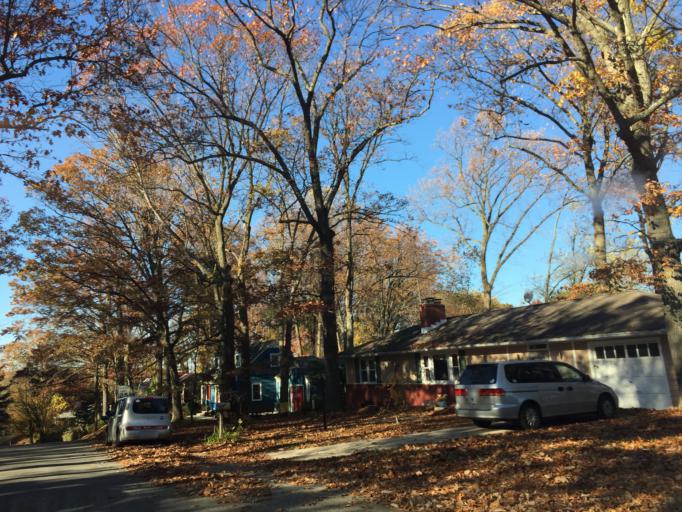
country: US
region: Maryland
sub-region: Baltimore County
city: Parkville
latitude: 39.4042
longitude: -76.5530
